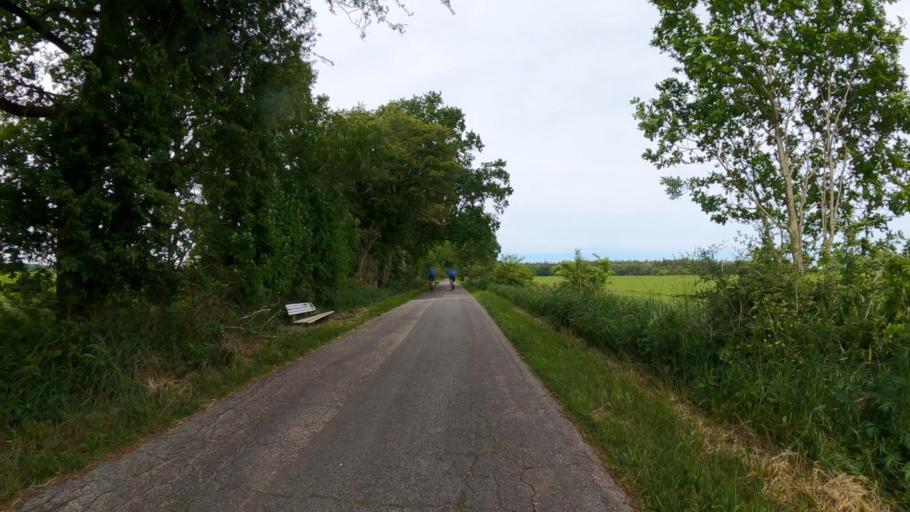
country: DE
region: Schleswig-Holstein
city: Hartenholm
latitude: 53.8862
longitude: 10.0805
